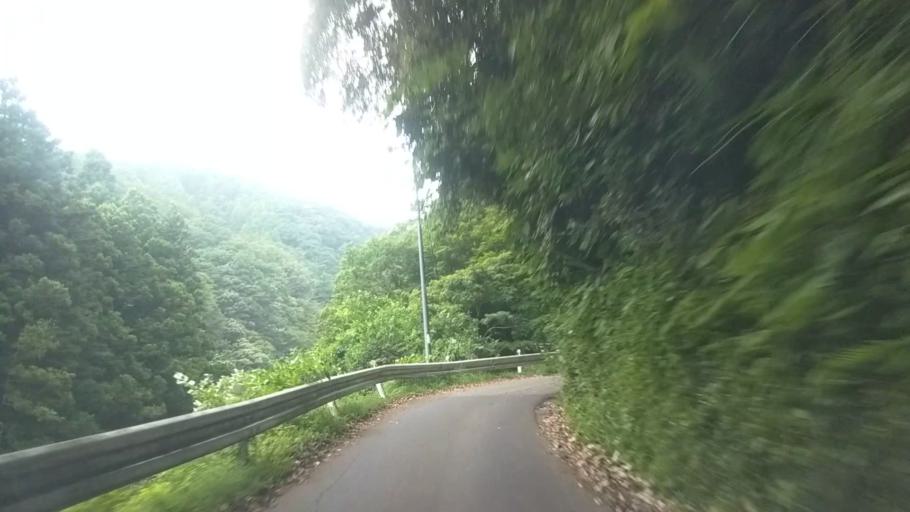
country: JP
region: Chiba
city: Kawaguchi
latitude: 35.2053
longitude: 140.1407
